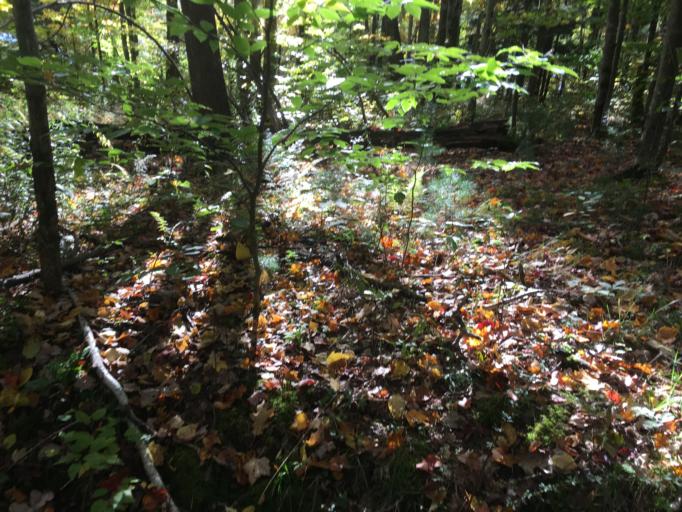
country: US
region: Pennsylvania
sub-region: Susquehanna County
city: Susquehanna
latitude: 42.0415
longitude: -75.6341
